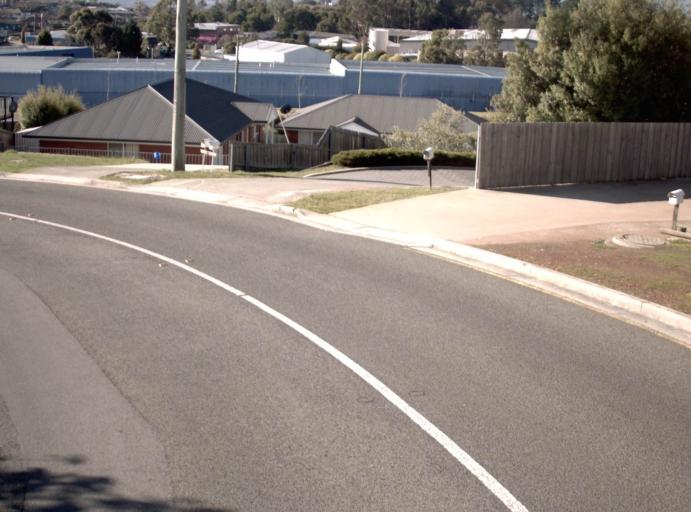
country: AU
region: Tasmania
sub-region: Launceston
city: Summerhill
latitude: -41.4734
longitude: 147.1345
